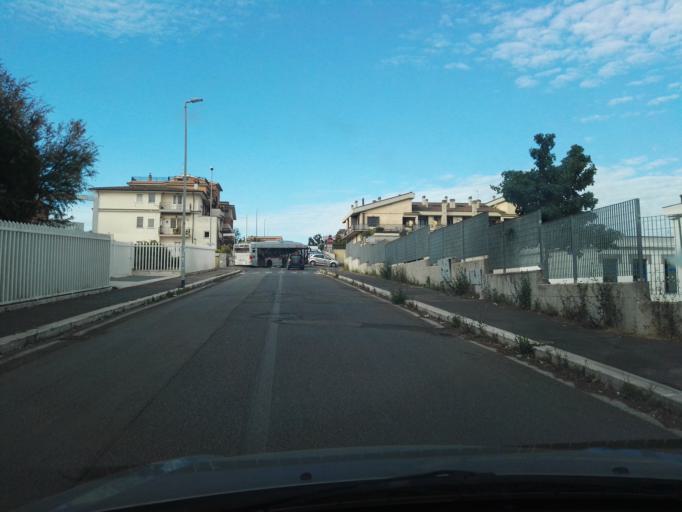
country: IT
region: Latium
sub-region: Citta metropolitana di Roma Capitale
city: Selcetta
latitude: 41.7662
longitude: 12.4744
